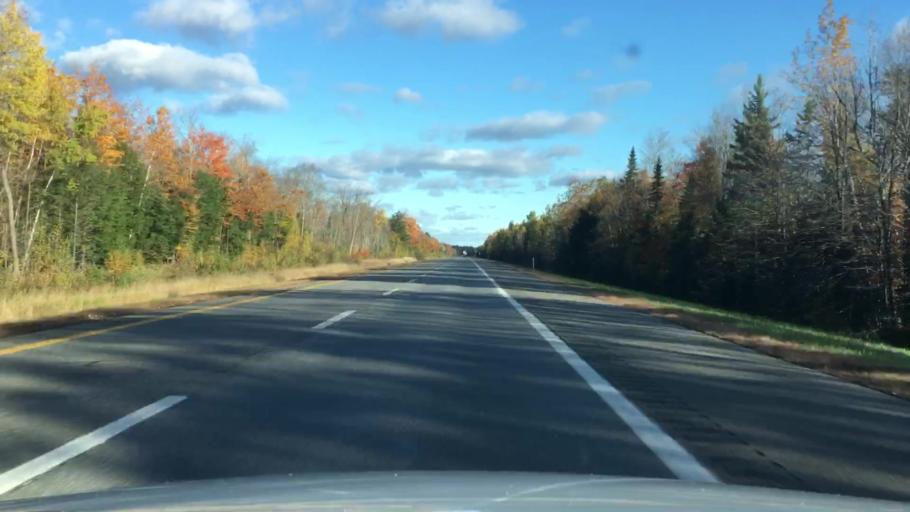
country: US
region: Maine
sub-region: Penobscot County
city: Greenbush
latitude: 45.0841
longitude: -68.6928
